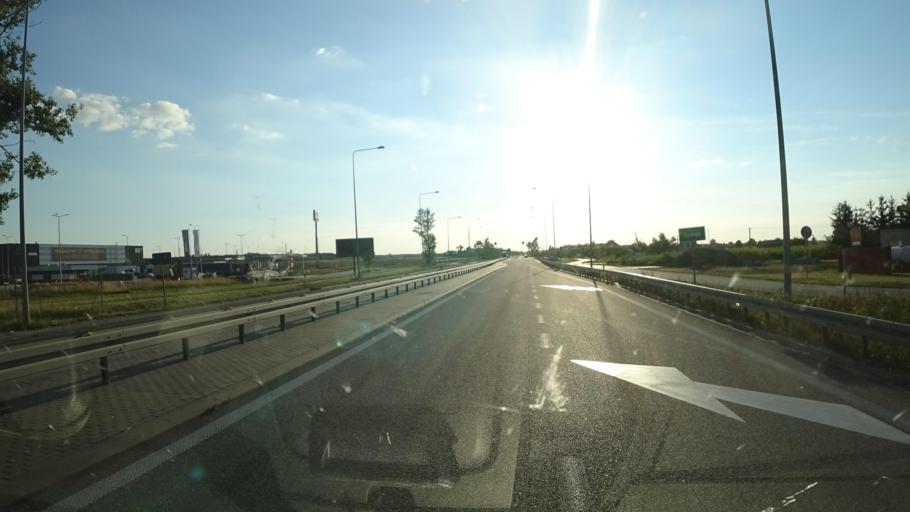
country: PL
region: Lodz Voivodeship
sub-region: Powiat kutnowski
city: Krzyzanow
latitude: 52.2196
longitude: 19.4655
